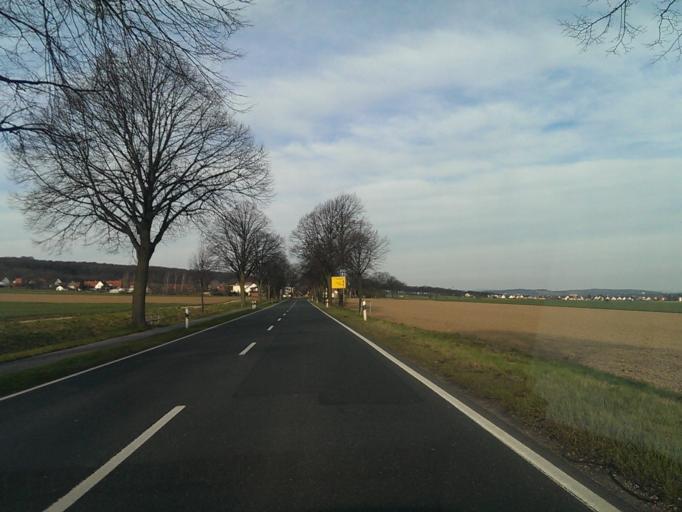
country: DE
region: Lower Saxony
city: Hildesheim
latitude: 52.1388
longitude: 10.0310
